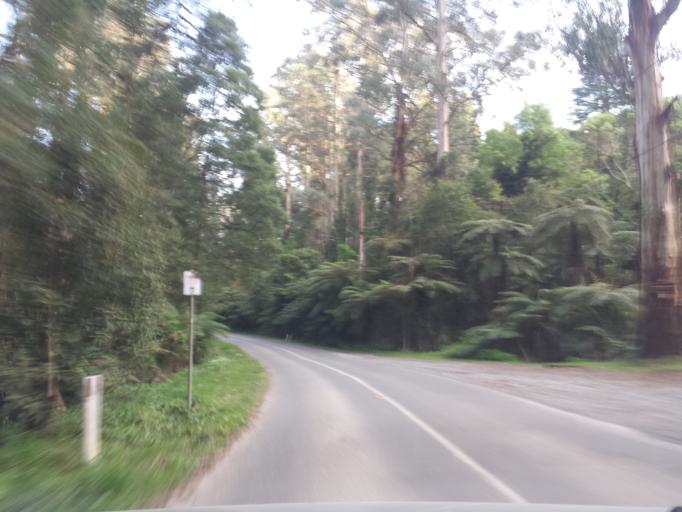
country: AU
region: Victoria
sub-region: Yarra Ranges
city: Kallista
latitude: -37.8738
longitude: 145.3713
